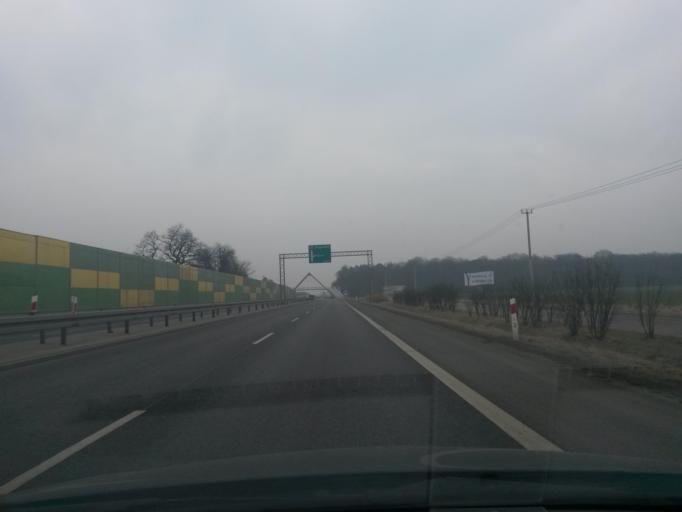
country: PL
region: Masovian Voivodeship
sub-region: Powiat legionowski
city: Serock
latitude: 52.4856
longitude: 21.0433
